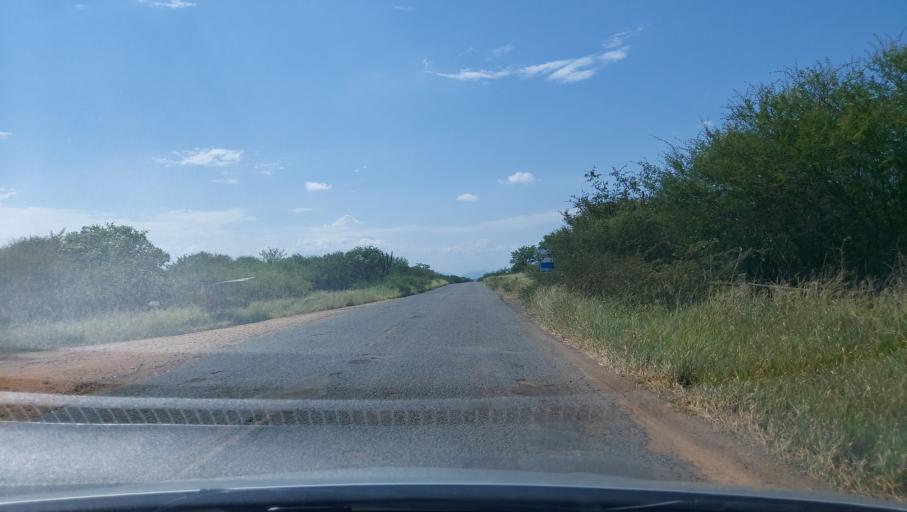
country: BR
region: Bahia
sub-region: Oliveira Dos Brejinhos
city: Beira Rio
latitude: -12.1639
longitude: -42.5485
